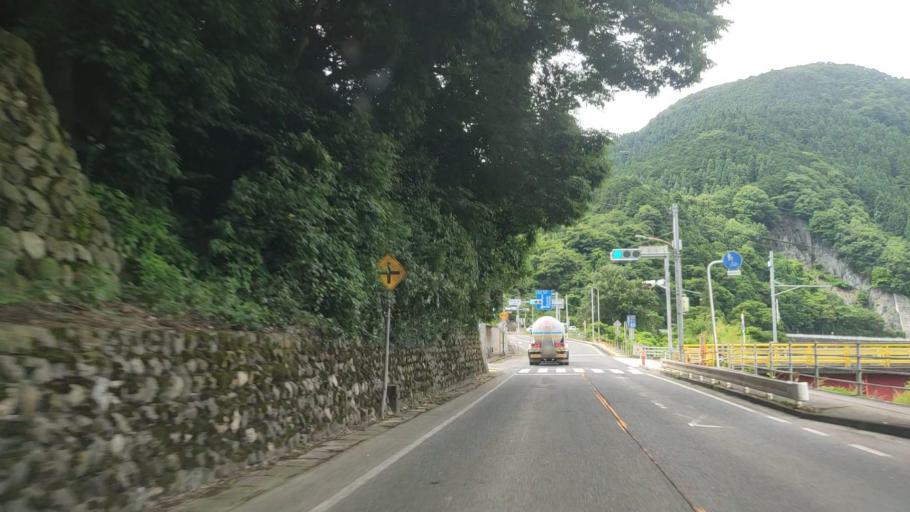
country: JP
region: Tottori
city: Yonago
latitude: 35.2374
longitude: 133.4397
